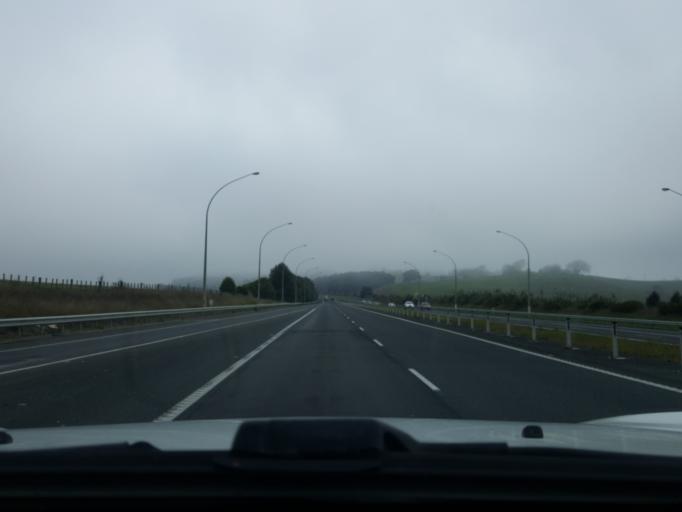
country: NZ
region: Waikato
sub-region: Waikato District
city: Te Kauwhata
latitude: -37.3535
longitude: 175.0816
